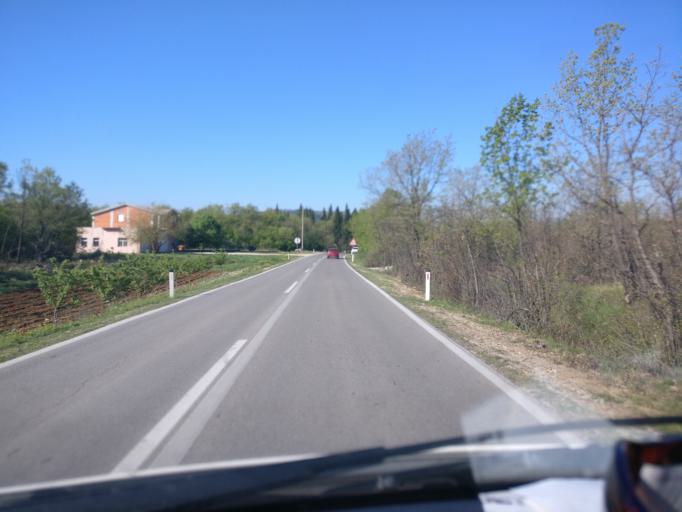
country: BA
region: Federation of Bosnia and Herzegovina
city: Tasovcici
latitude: 43.1277
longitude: 17.7631
